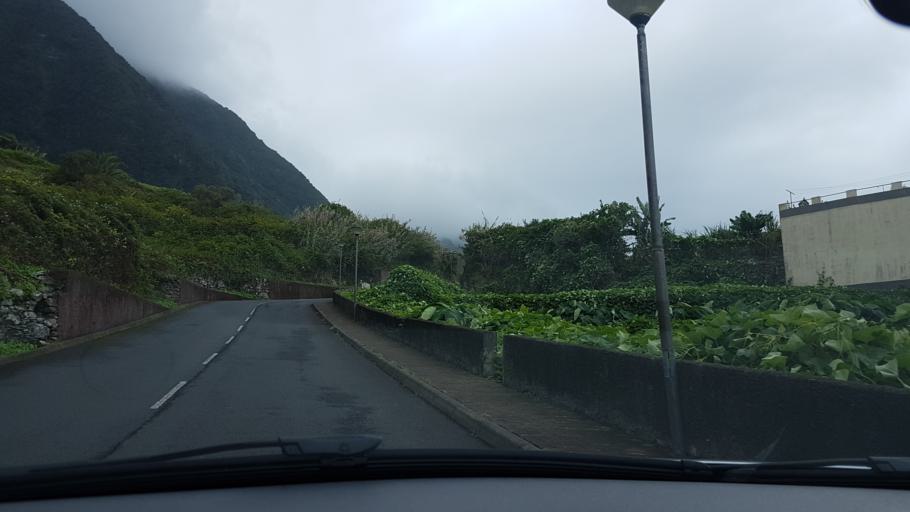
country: PT
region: Madeira
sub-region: Sao Vicente
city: Sao Vicente
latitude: 32.8254
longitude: -16.9872
